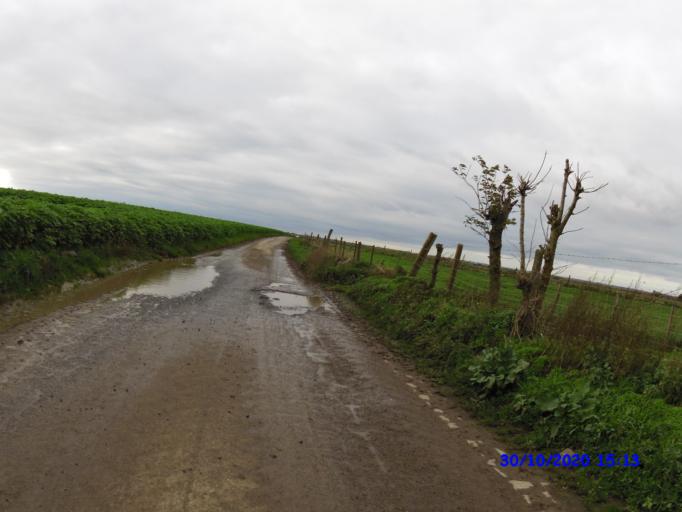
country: BE
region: Flanders
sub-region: Provincie Vlaams-Brabant
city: Landen
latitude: 50.7541
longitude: 5.0412
